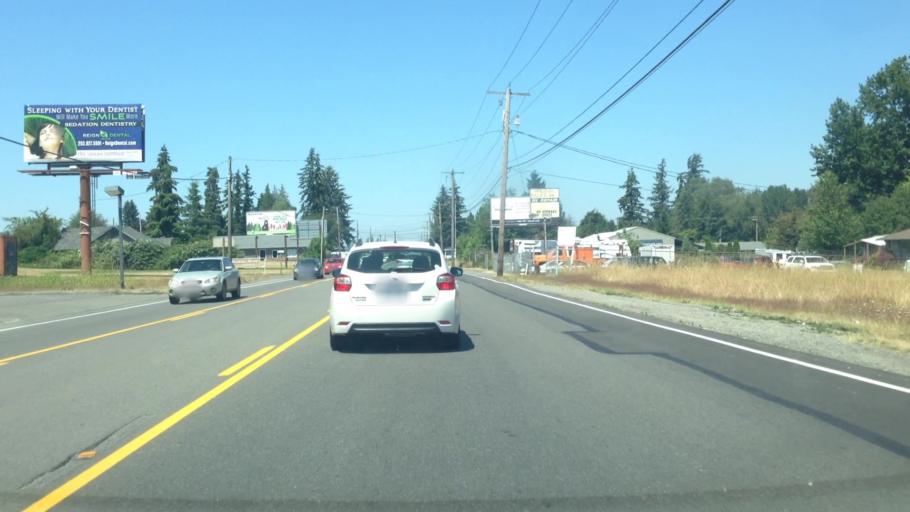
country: US
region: Washington
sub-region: Pierce County
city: North Puyallup
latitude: 47.2261
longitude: -122.2940
